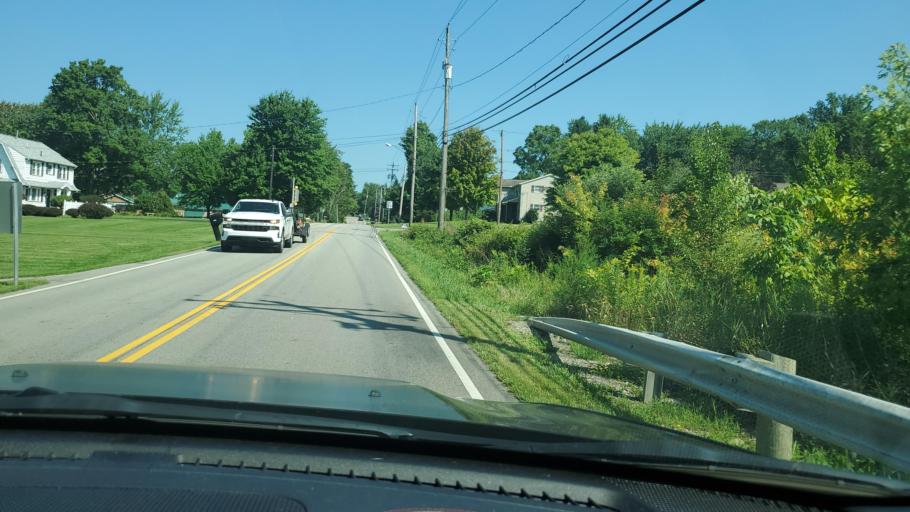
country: US
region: Ohio
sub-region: Trumbull County
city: Girard
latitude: 41.1721
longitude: -80.6908
